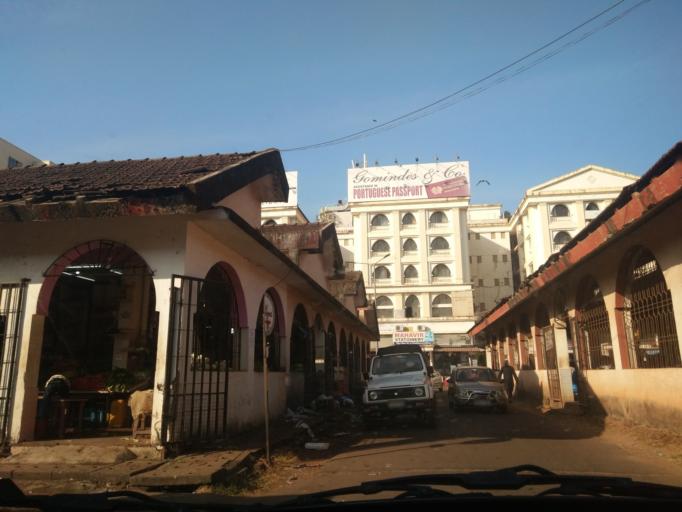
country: IN
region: Goa
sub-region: South Goa
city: Madgaon
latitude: 15.2857
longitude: 73.9581
